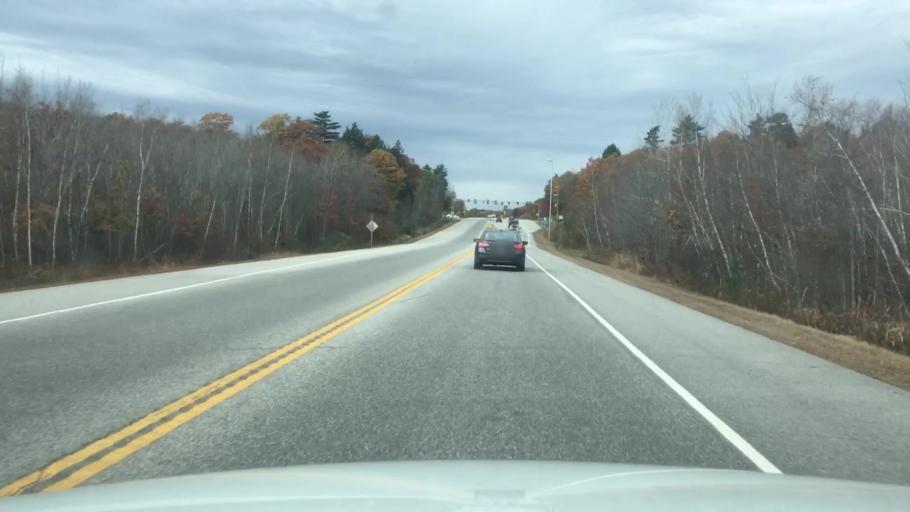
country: US
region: Maine
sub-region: Cumberland County
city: Brunswick
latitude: 43.9349
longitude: -69.9530
